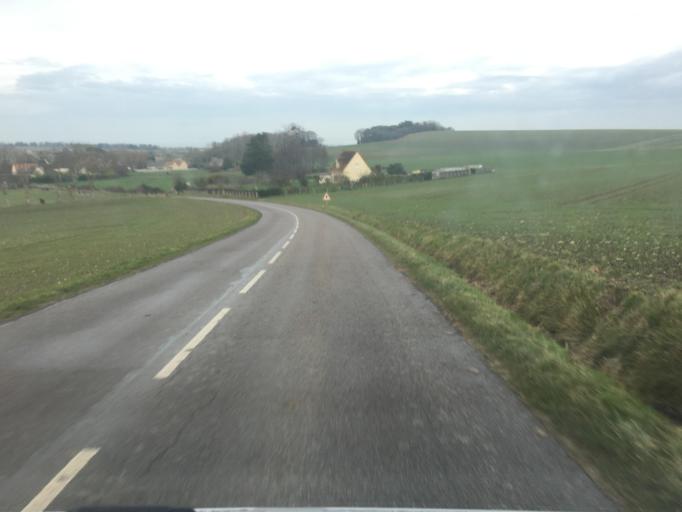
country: FR
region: Lower Normandy
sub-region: Departement du Calvados
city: Ver-sur-Mer
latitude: 49.3241
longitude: -0.5595
